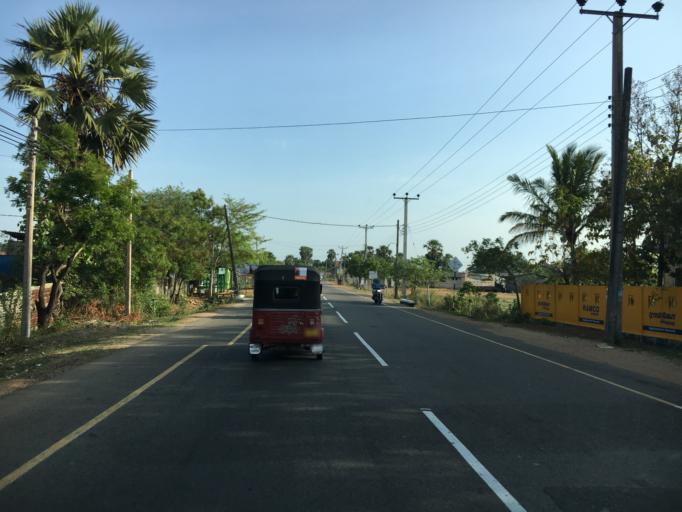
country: LK
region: Eastern Province
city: Eravur Town
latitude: 7.9263
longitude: 81.5135
